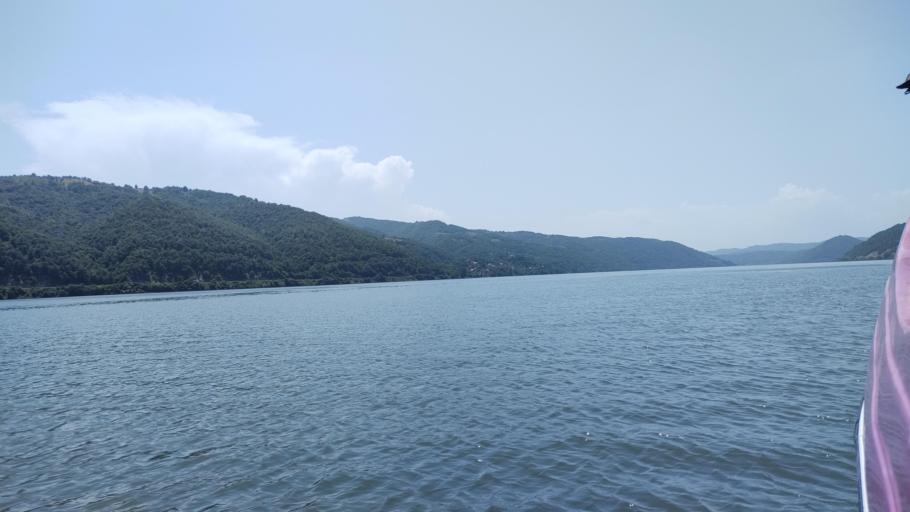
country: RO
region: Mehedinti
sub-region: Comuna Svinita
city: Svinita
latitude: 44.5200
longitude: 22.2013
